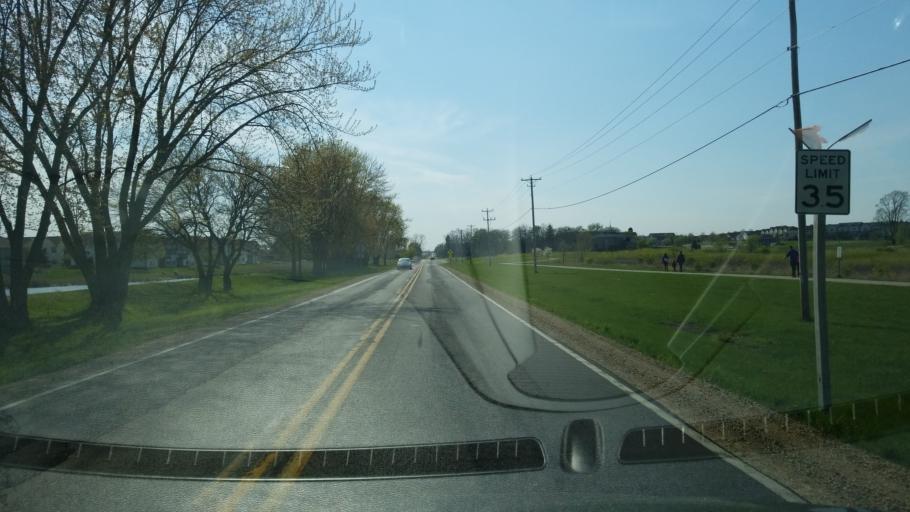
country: US
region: Wisconsin
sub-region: Dane County
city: Oregon
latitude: 42.9290
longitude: -89.3958
